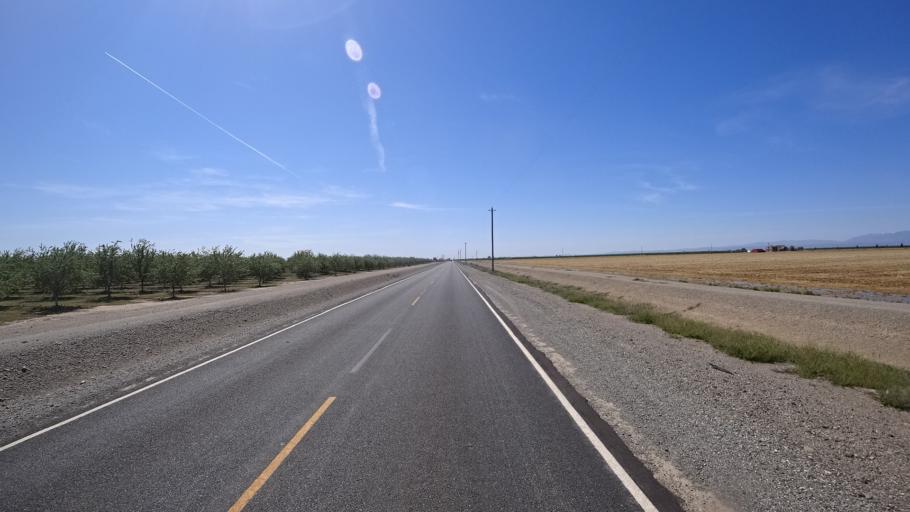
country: US
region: California
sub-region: Glenn County
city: Orland
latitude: 39.6597
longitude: -122.1407
